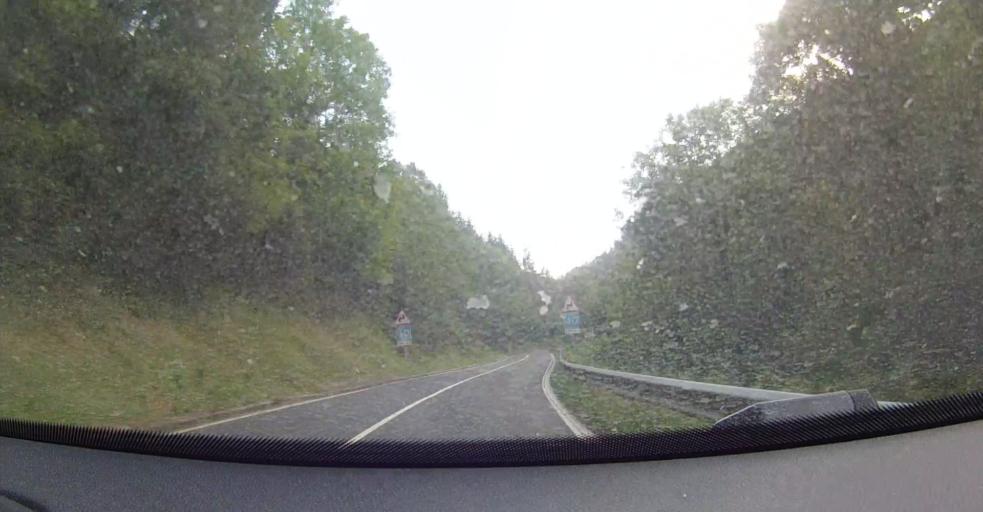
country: ES
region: Basque Country
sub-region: Bizkaia
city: Urrestieta
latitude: 43.2420
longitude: -3.1557
